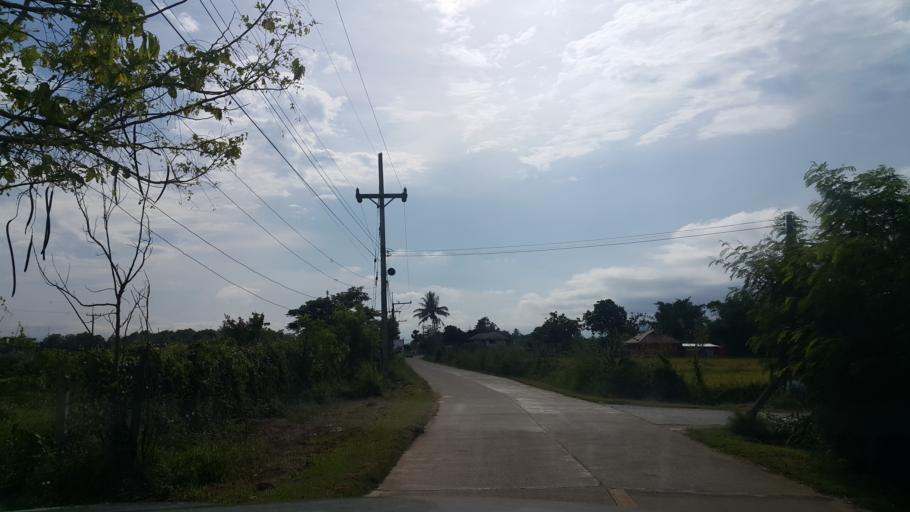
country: TH
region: Chiang Rai
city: Chiang Rai
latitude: 19.9714
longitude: 99.8916
